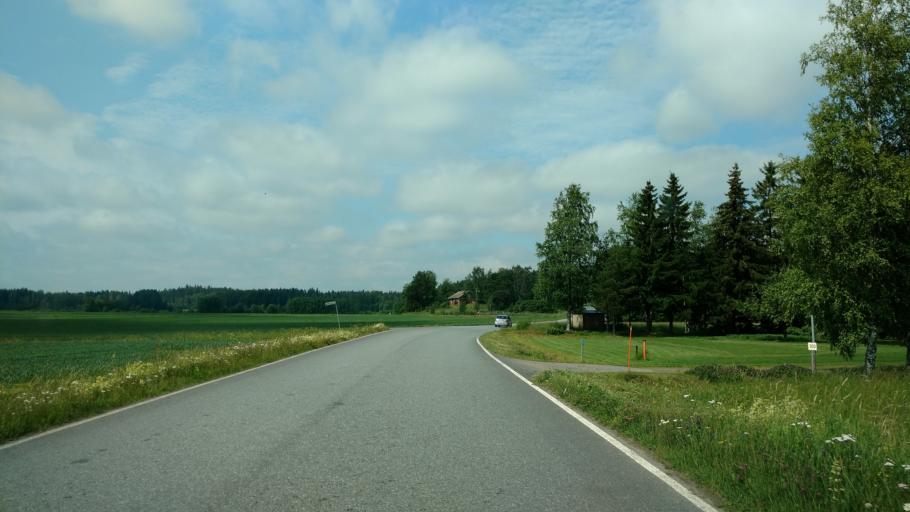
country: FI
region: Haeme
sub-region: Forssa
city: Ypaejae
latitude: 60.8029
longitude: 23.3329
